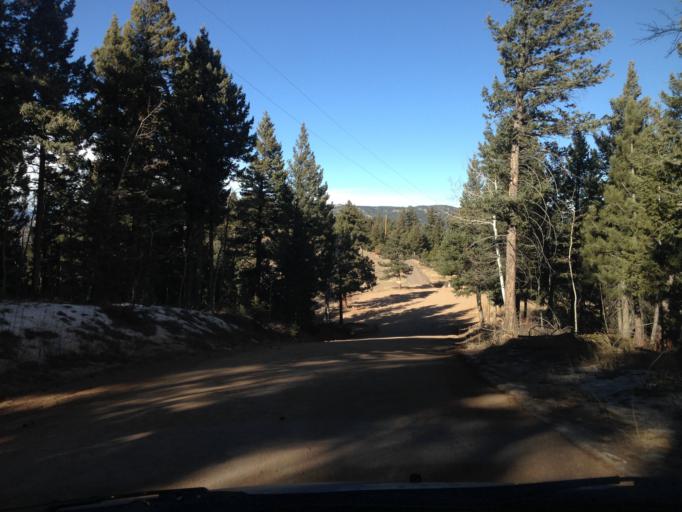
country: US
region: Colorado
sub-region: Boulder County
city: Coal Creek
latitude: 39.9226
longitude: -105.3526
